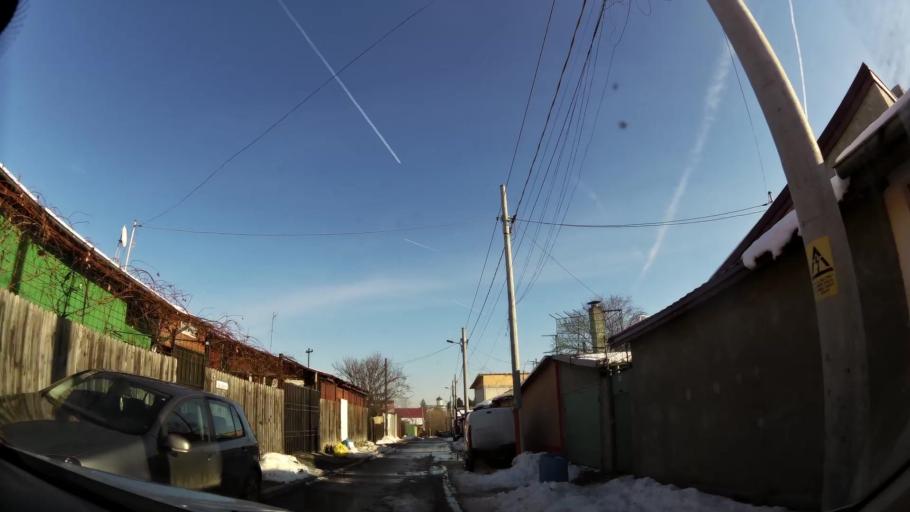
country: RO
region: Ilfov
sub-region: Comuna Fundeni-Dobroesti
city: Fundeni
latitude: 44.4728
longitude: 26.1300
